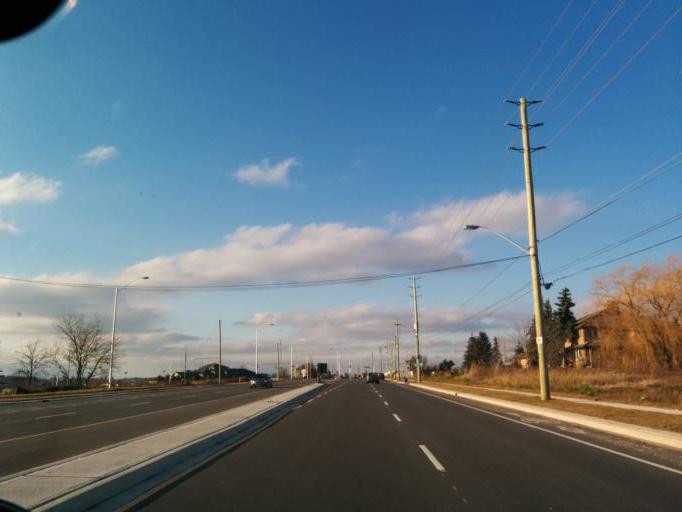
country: CA
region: Ontario
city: Oakville
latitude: 43.5064
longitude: -79.6947
